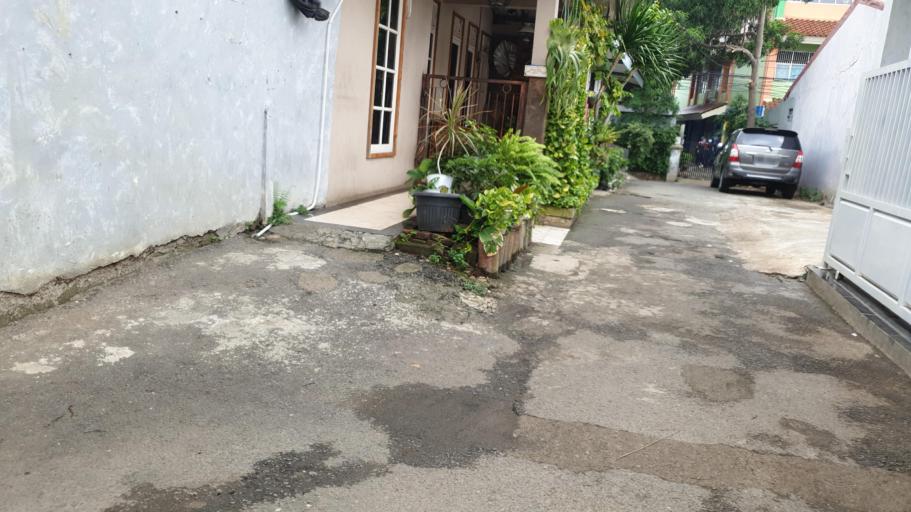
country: ID
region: Banten
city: South Tangerang
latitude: -6.2565
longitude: 106.7827
